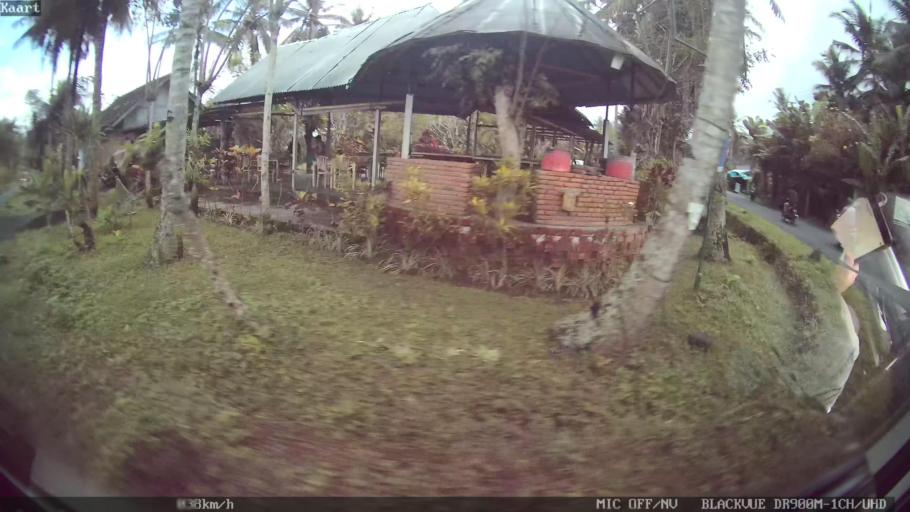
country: ID
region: Bali
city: Banjar Parekan
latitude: -8.5700
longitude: 115.2093
